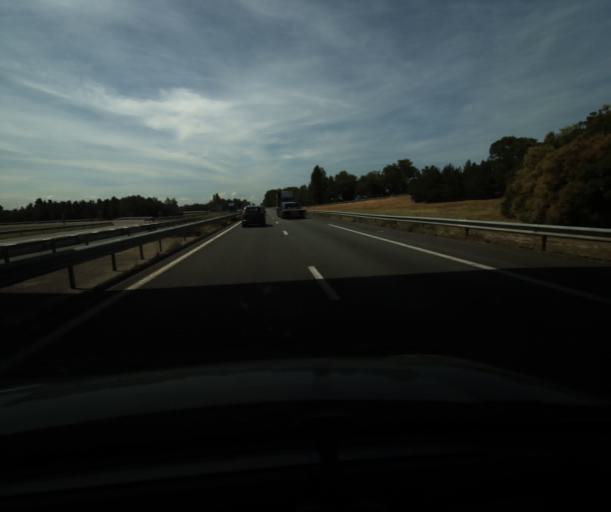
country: FR
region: Languedoc-Roussillon
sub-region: Departement de l'Aude
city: Bram
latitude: 43.2365
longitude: 2.0975
